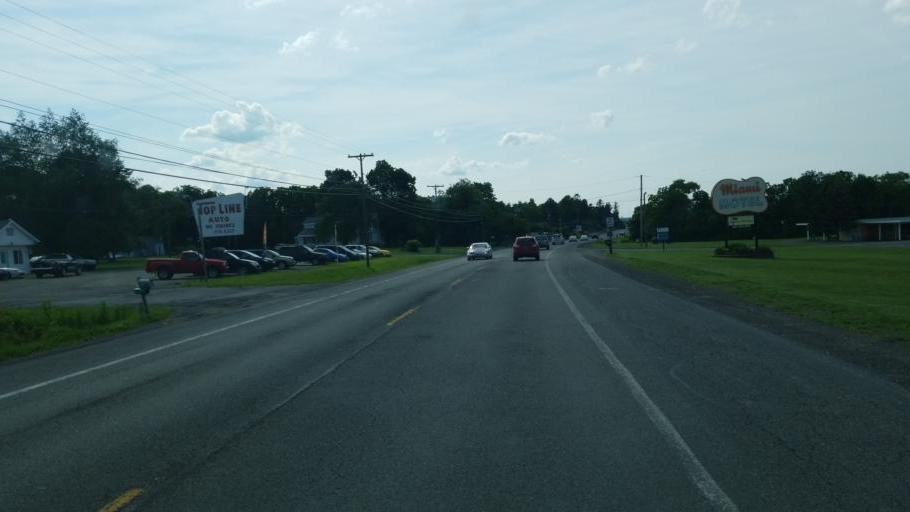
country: US
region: New York
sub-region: Ontario County
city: Canandaigua
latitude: 42.8669
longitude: -77.2282
